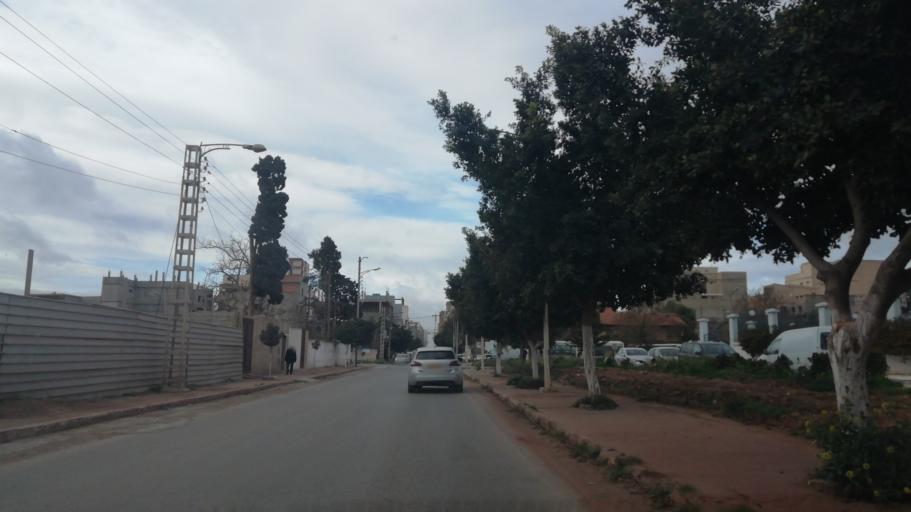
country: DZ
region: Oran
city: Bir el Djir
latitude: 35.7202
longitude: -0.5660
